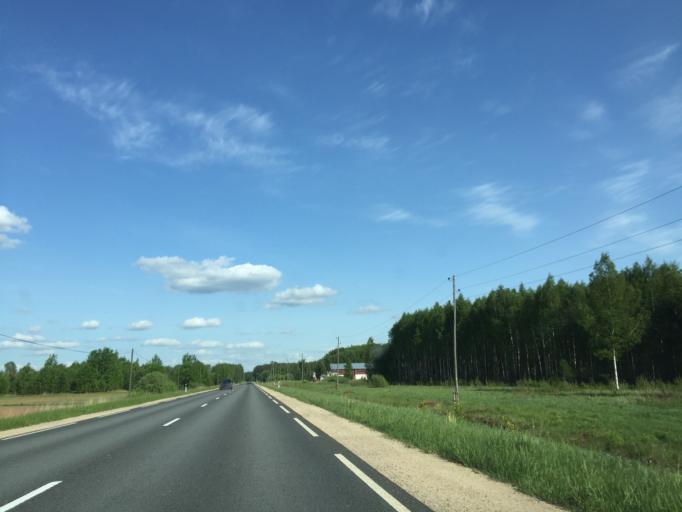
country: LV
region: Salaspils
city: Salaspils
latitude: 56.8246
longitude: 24.3761
